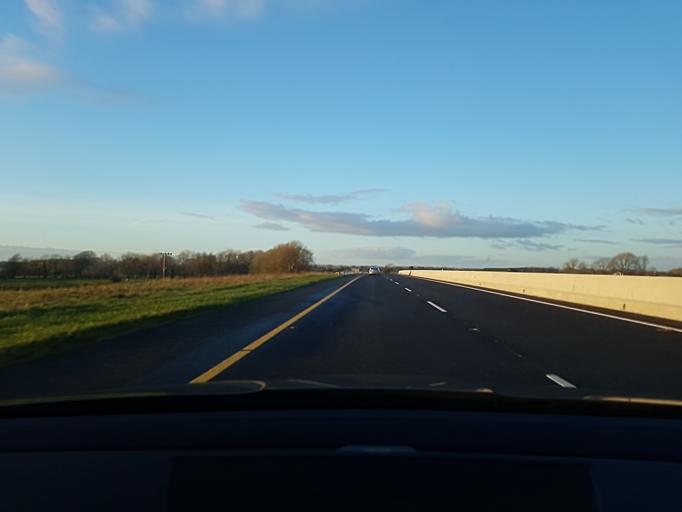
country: IE
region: Connaught
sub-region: County Galway
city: Athenry
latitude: 53.3174
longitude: -8.8012
